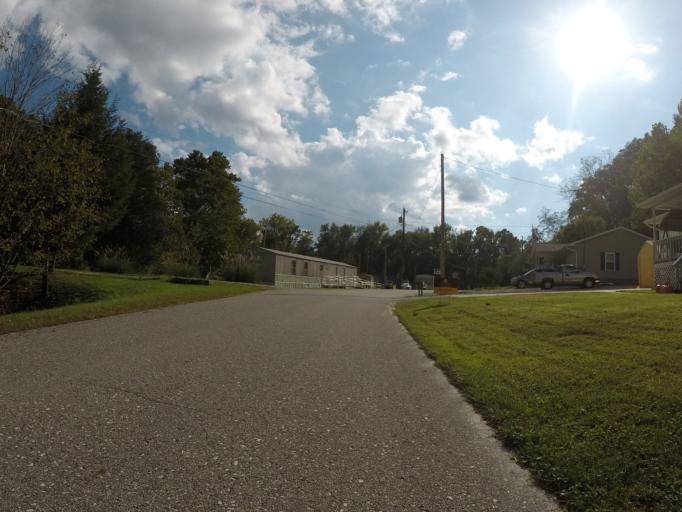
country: US
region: West Virginia
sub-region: Wayne County
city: Lavalette
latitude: 38.3508
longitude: -82.4934
